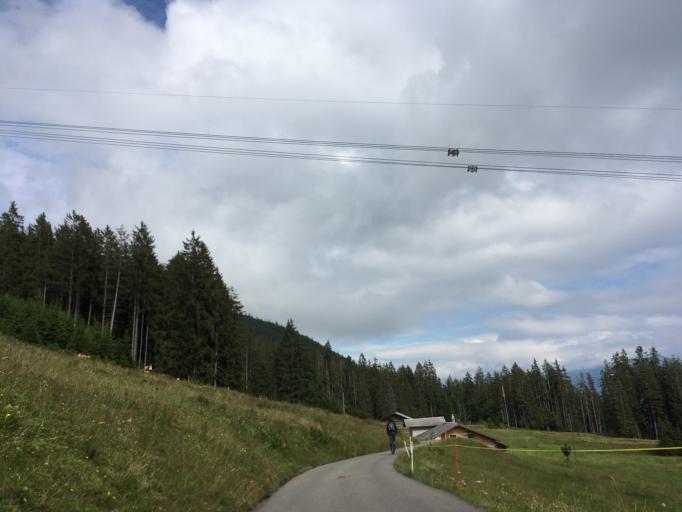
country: CH
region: Bern
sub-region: Interlaken-Oberhasli District
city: Beatenberg
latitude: 46.6966
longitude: 7.7674
